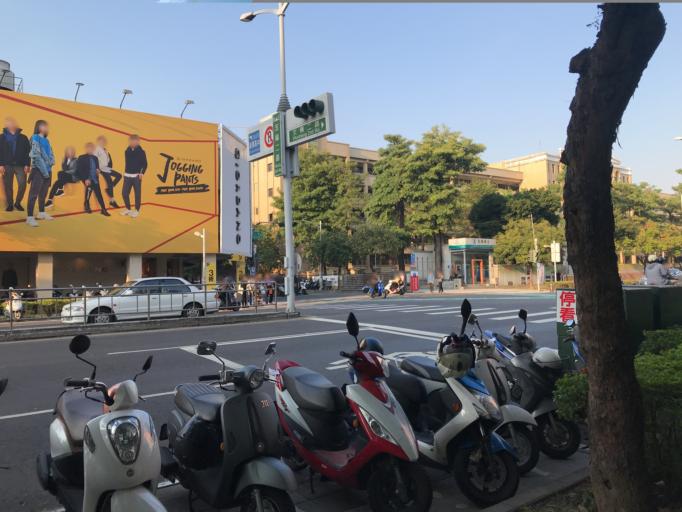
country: TW
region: Kaohsiung
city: Kaohsiung
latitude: 22.6240
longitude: 120.3032
